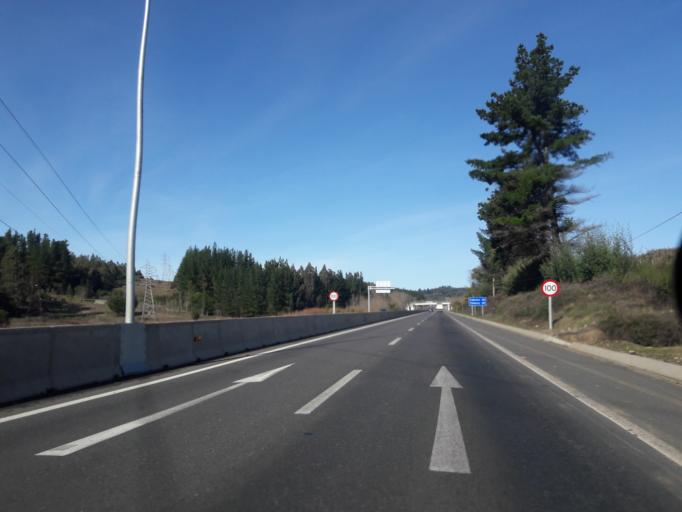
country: CL
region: Biobio
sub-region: Provincia de Concepcion
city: Chiguayante
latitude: -36.9123
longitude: -72.7772
